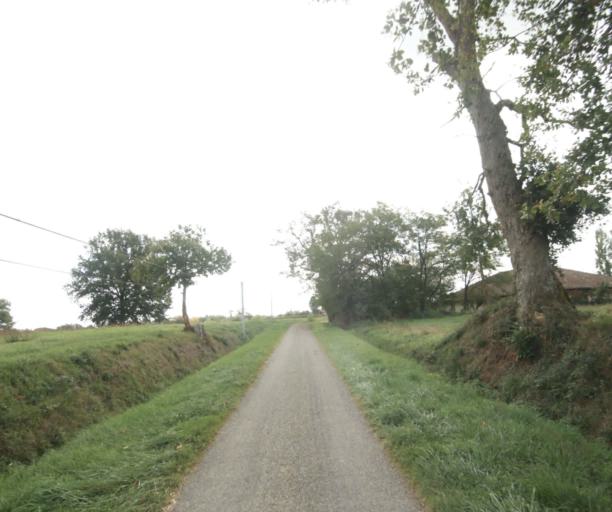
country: FR
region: Midi-Pyrenees
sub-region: Departement du Gers
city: Eauze
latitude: 43.8387
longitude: 0.1181
